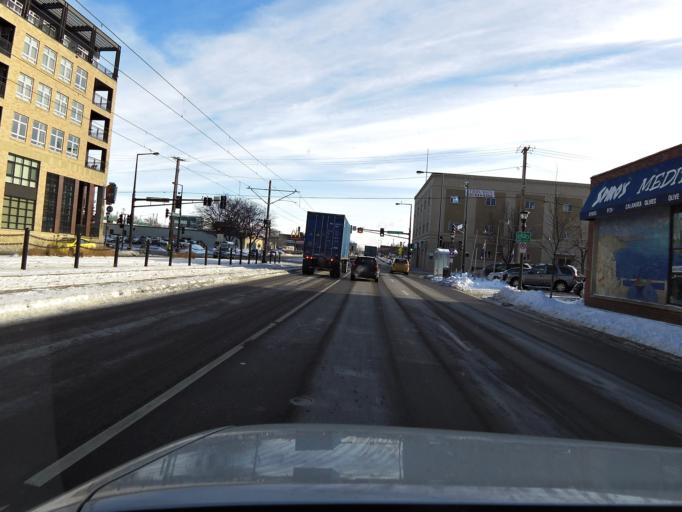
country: US
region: Minnesota
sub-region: Ramsey County
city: Lauderdale
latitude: 44.9623
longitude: -93.1936
